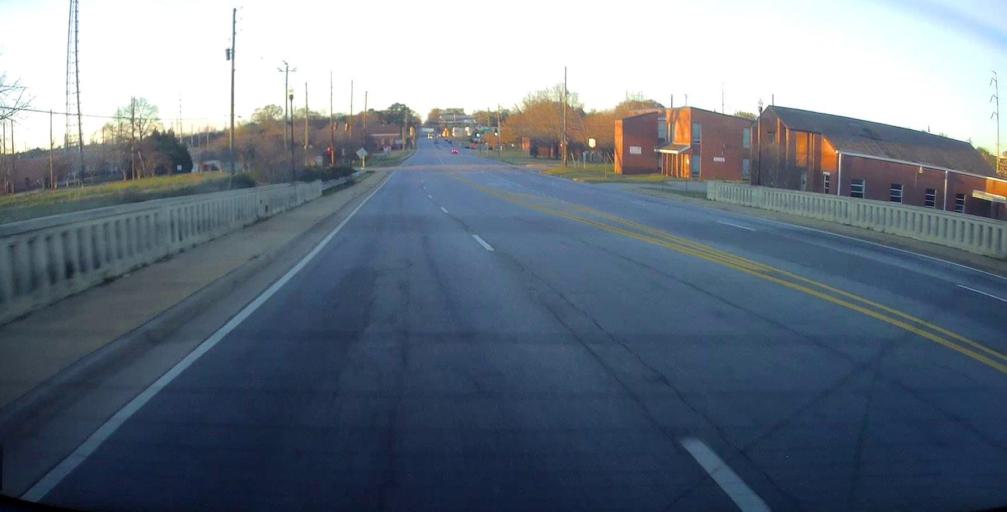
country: US
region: Alabama
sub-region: Russell County
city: Phenix City
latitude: 32.4789
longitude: -84.9904
